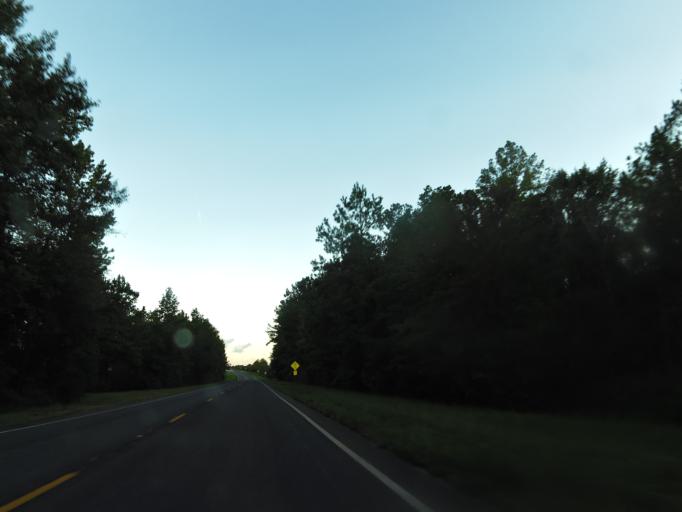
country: US
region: Georgia
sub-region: Camden County
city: Woodbine
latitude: 30.9810
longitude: -81.7275
